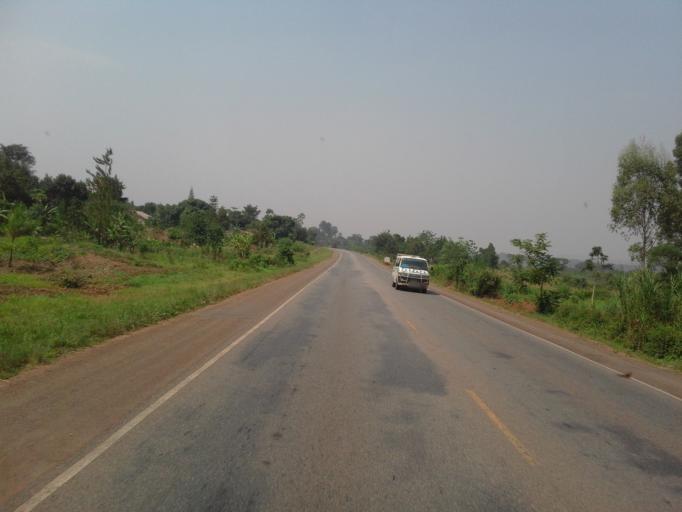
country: UG
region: Eastern Region
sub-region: Iganga District
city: Iganga
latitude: 0.5862
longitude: 33.4370
